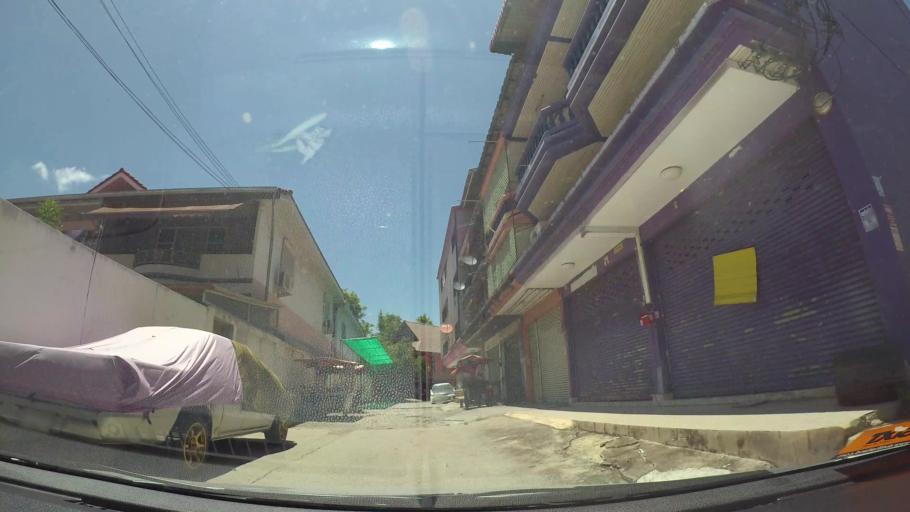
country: TH
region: Chon Buri
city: Phatthaya
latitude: 12.9193
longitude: 100.8957
